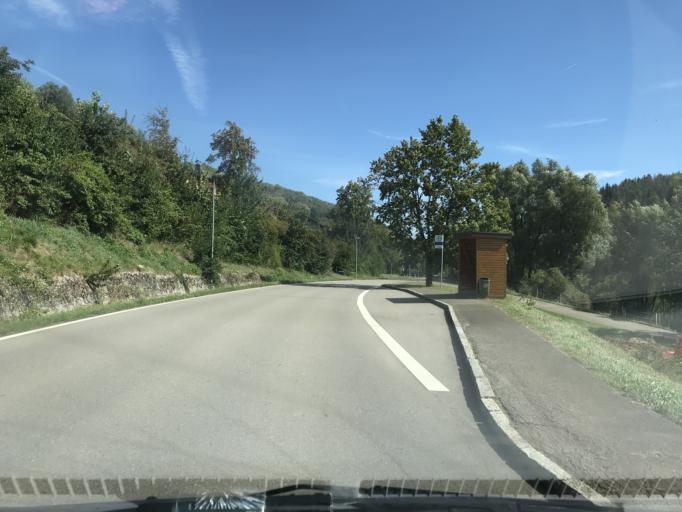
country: DE
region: Baden-Wuerttemberg
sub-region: Freiburg Region
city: Schworstadt
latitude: 47.6142
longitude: 7.8599
